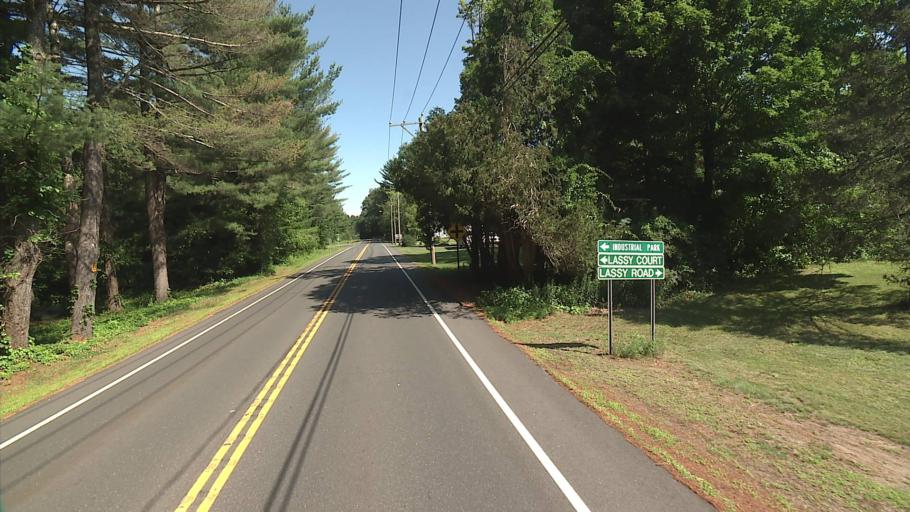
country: US
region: Connecticut
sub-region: Litchfield County
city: Terryville
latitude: 41.7006
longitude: -73.0074
